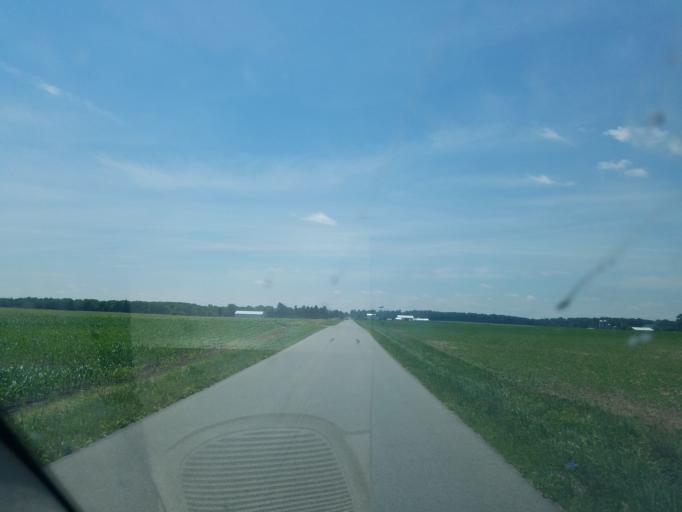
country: US
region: Ohio
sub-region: Hancock County
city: Arlington
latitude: 40.8566
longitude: -83.7085
